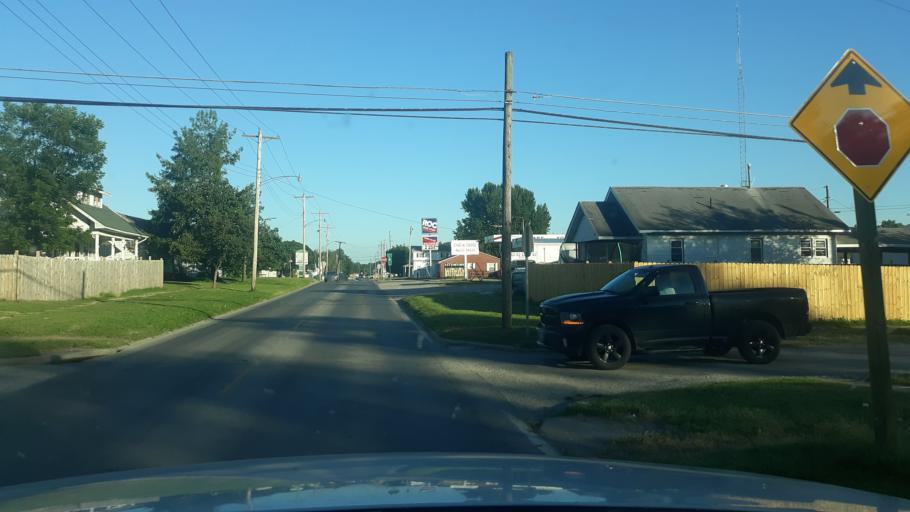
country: US
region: Illinois
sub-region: Saline County
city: Eldorado
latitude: 37.8126
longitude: -88.4439
